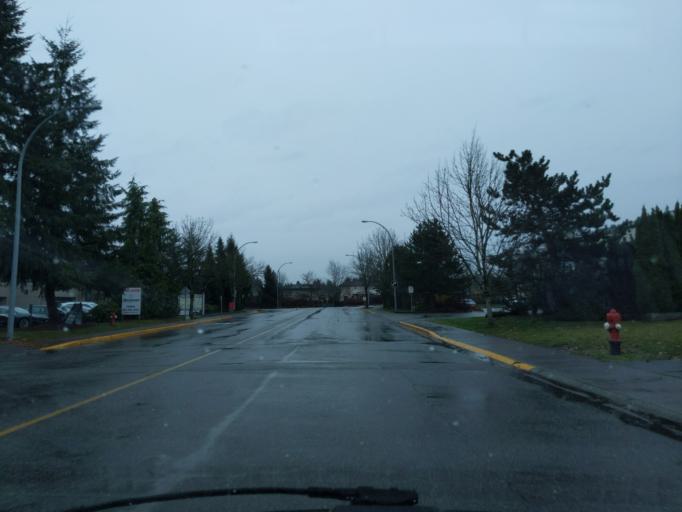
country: CA
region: British Columbia
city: Walnut Grove
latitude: 49.1708
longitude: -122.6649
